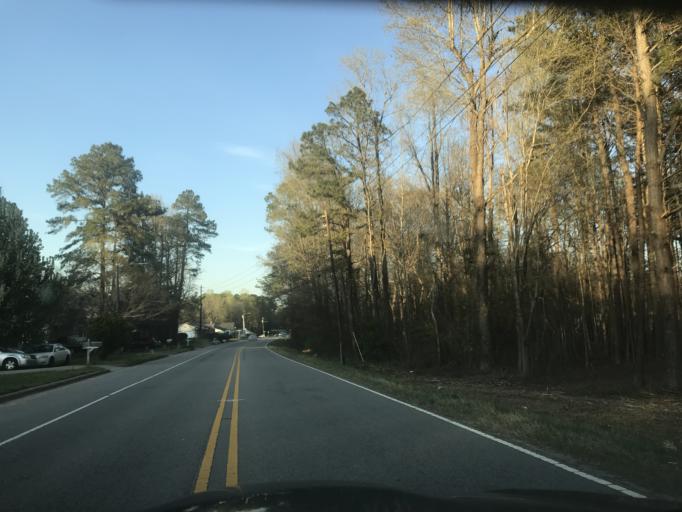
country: US
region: North Carolina
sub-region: Wake County
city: Knightdale
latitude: 35.7438
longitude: -78.5387
